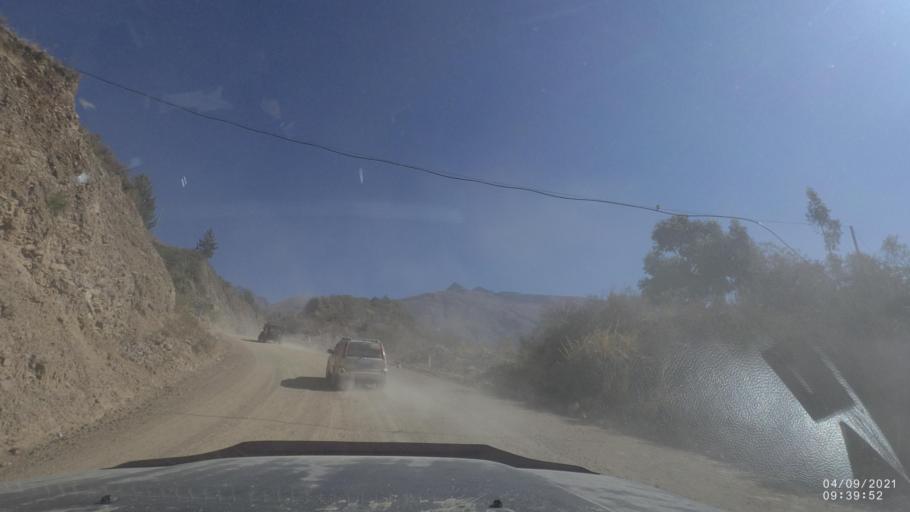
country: BO
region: Cochabamba
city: Sipe Sipe
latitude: -17.3444
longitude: -66.3859
